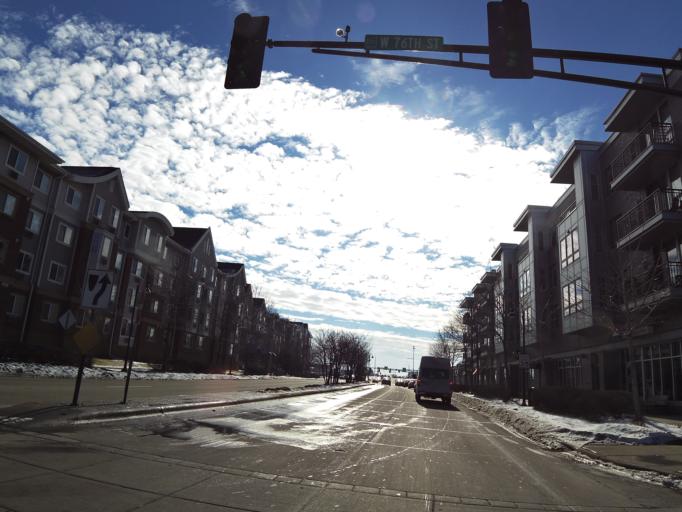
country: US
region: Minnesota
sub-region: Hennepin County
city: Richfield
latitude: 44.8656
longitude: -93.2885
